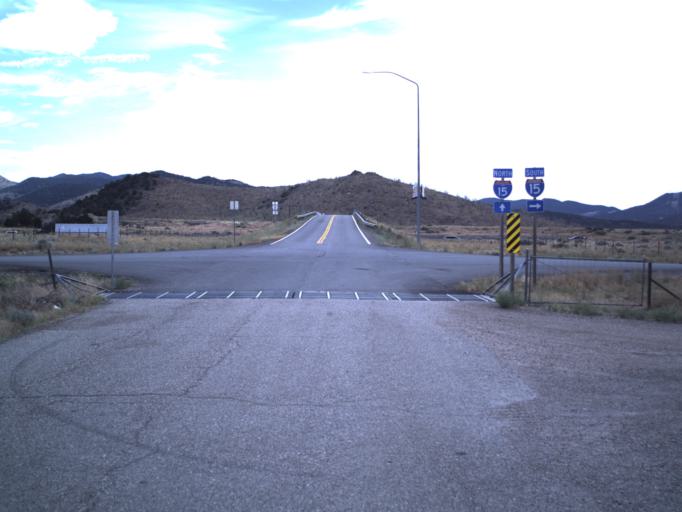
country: US
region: Utah
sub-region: Beaver County
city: Beaver
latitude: 38.6158
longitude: -112.6123
